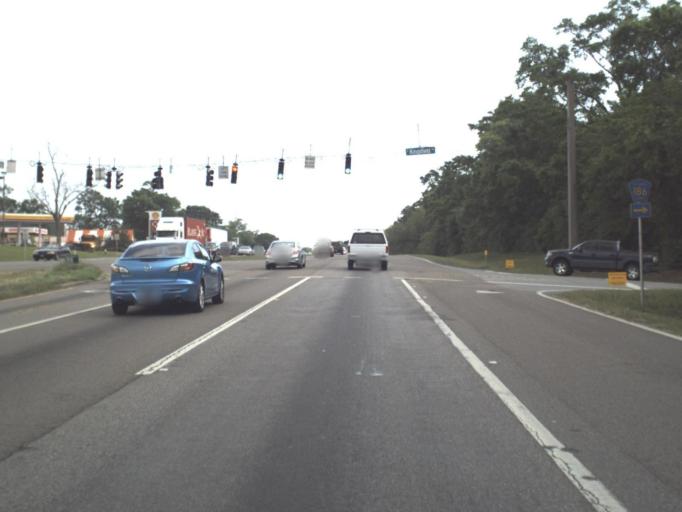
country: US
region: Florida
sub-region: Escambia County
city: Gonzalez
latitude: 30.5705
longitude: -87.2909
